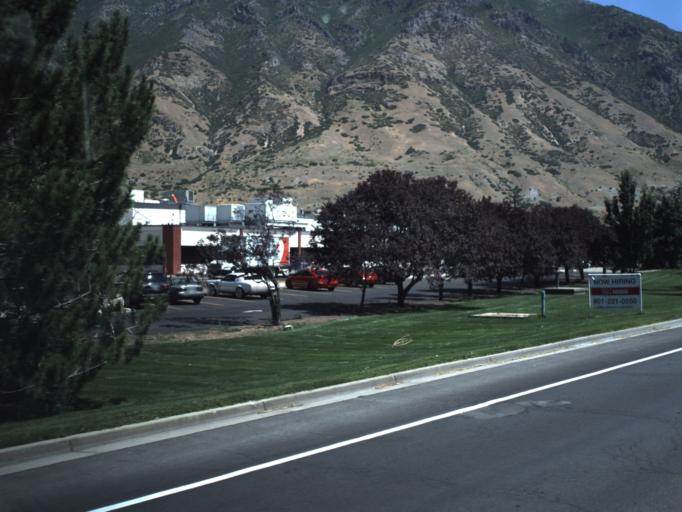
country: US
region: Utah
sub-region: Utah County
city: Springville
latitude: 40.1870
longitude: -111.6261
